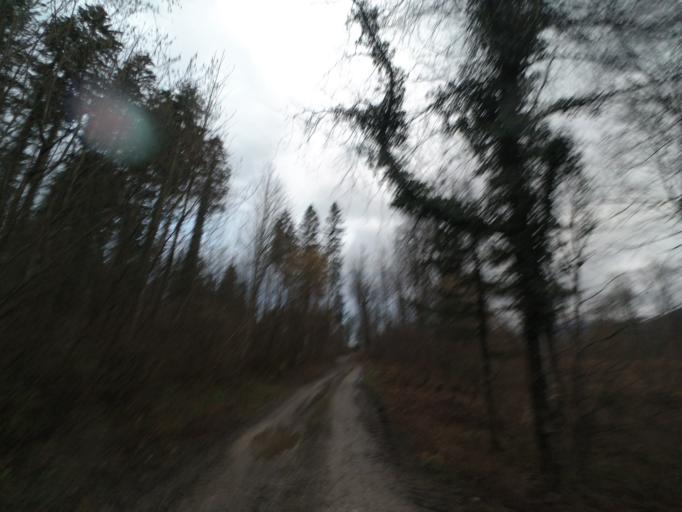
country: AT
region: Salzburg
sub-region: Politischer Bezirk Salzburg-Umgebung
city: Elsbethen
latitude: 47.7400
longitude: 13.0777
